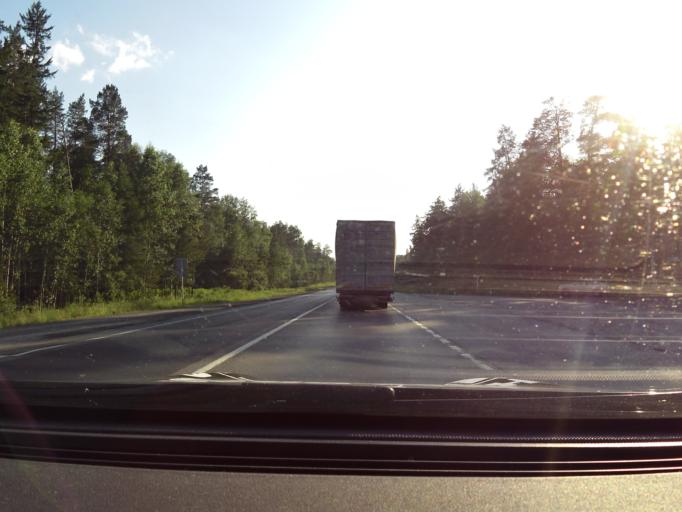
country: RU
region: Sverdlovsk
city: Druzhinino
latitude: 56.8383
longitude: 59.6543
